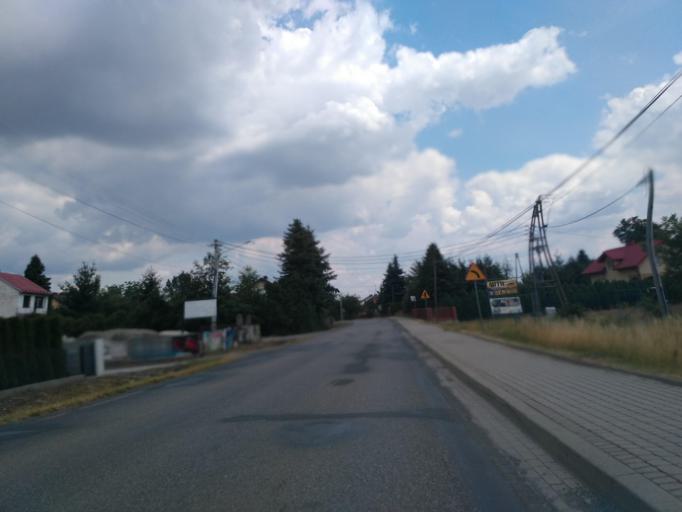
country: PL
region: Subcarpathian Voivodeship
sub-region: Powiat debicki
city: Pilzno
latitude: 50.0424
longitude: 21.3317
